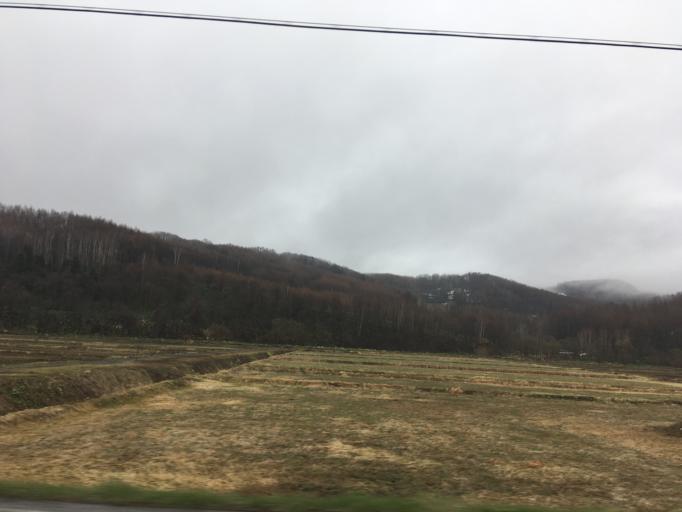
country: JP
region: Hokkaido
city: Nayoro
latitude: 44.0853
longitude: 142.4200
